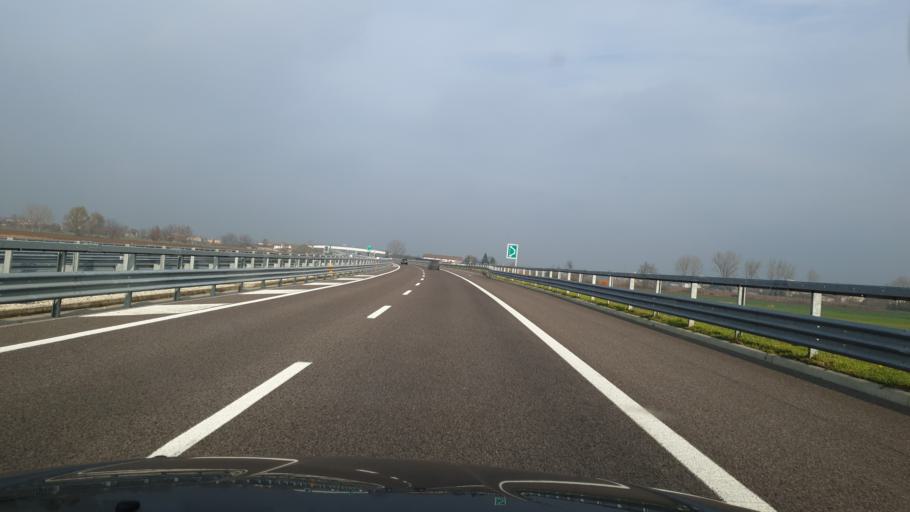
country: IT
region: Veneto
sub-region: Provincia di Padova
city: Megliadino San Vitale
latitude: 45.1933
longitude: 11.5430
